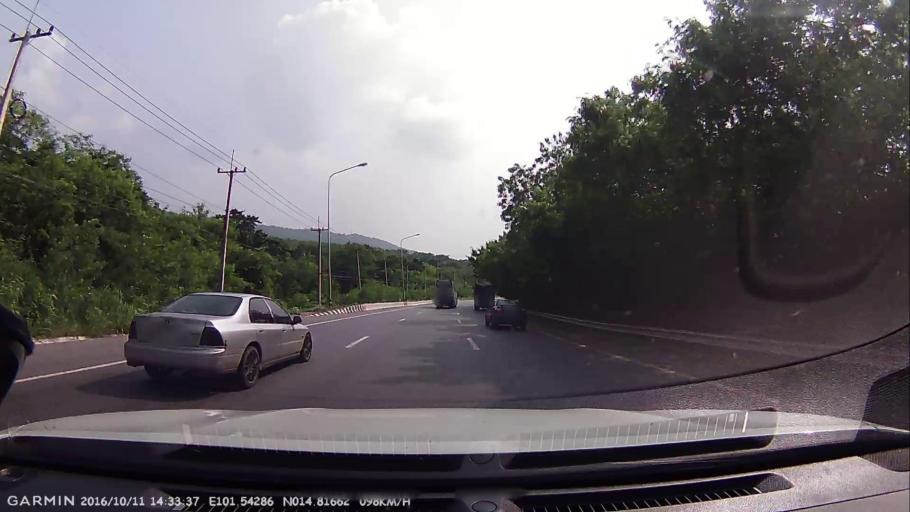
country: TH
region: Nakhon Ratchasima
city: Pak Chong
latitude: 14.8166
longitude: 101.5429
